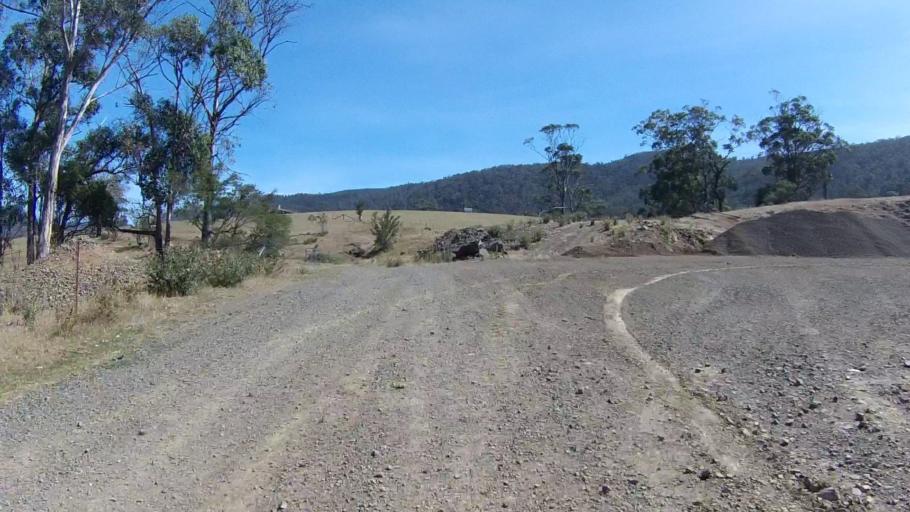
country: AU
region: Tasmania
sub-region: Sorell
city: Sorell
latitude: -42.7145
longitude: 147.5944
